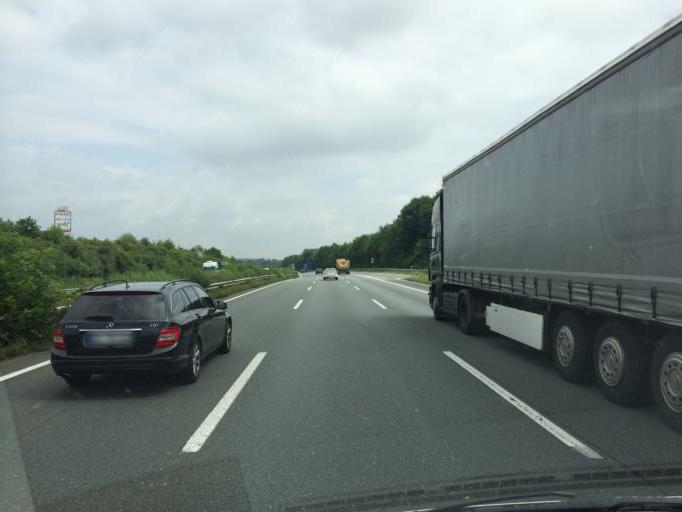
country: DE
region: North Rhine-Westphalia
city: Porta Westfalica
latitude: 52.2110
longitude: 8.8788
